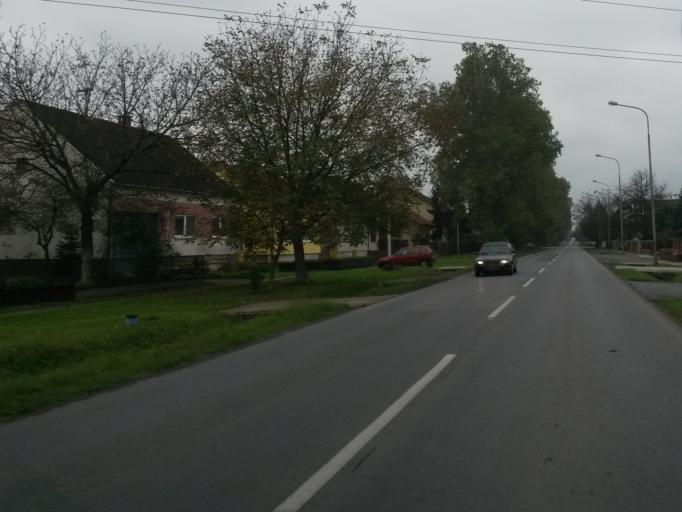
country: HR
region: Osjecko-Baranjska
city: Visnjevac
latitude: 45.5295
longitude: 18.6114
